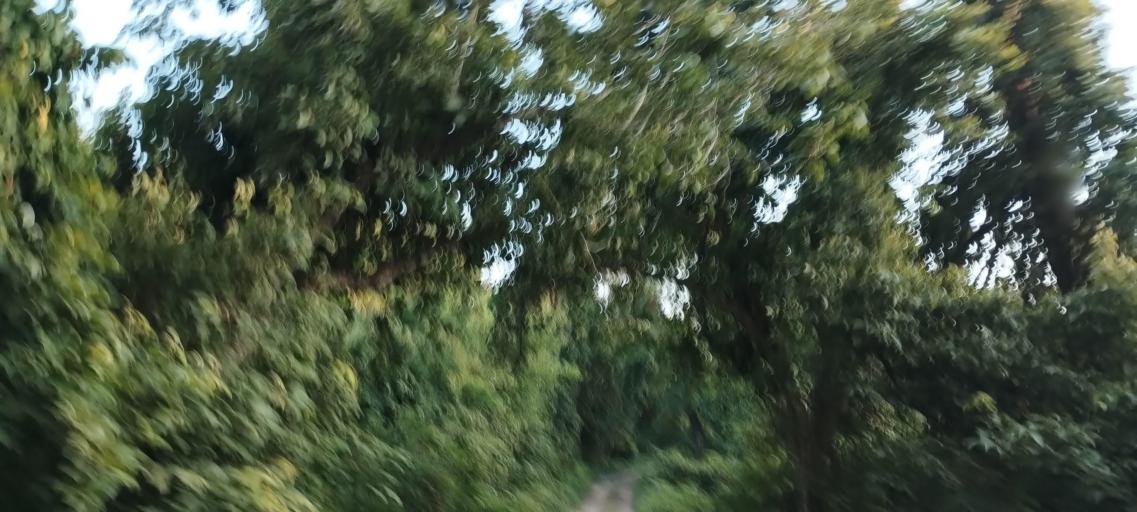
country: NP
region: Far Western
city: Tikapur
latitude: 28.4567
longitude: 81.2423
